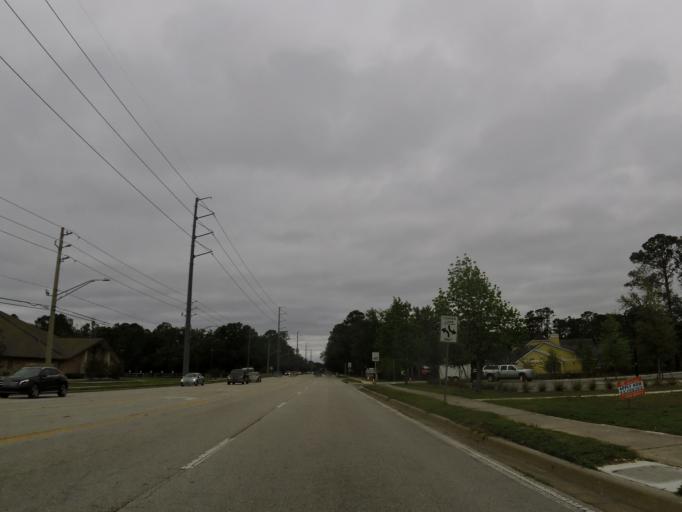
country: US
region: Florida
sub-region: Saint Johns County
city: Fruit Cove
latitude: 30.1771
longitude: -81.6048
